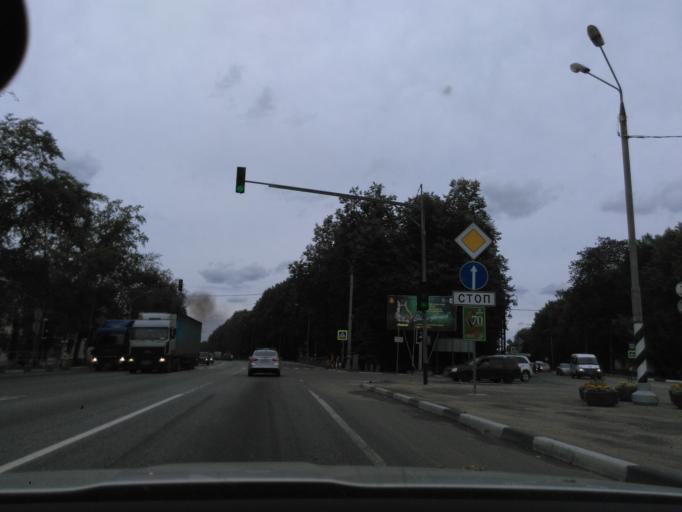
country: RU
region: Moskovskaya
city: Klin
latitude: 56.3266
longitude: 36.7522
